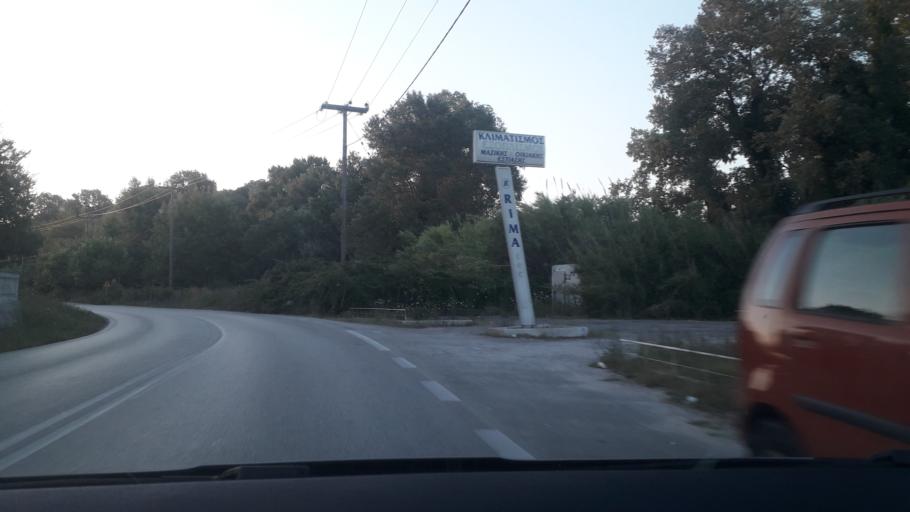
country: GR
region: Ionian Islands
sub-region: Nomos Kerkyras
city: Agios Matthaios
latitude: 39.4769
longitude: 19.9194
